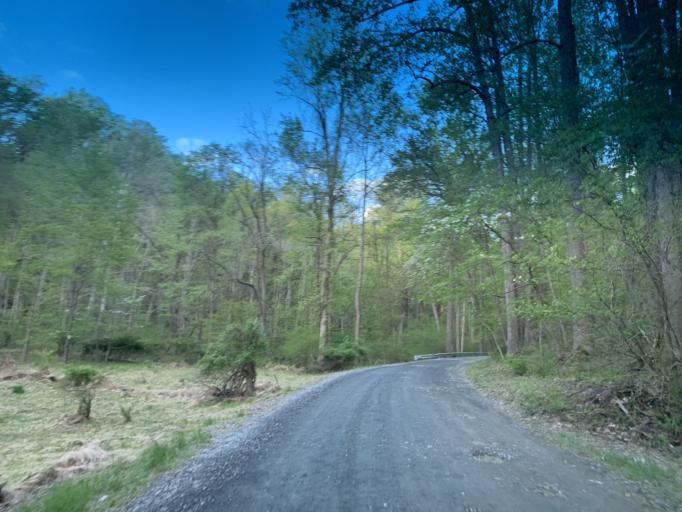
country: US
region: Maryland
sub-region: Harford County
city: Jarrettsville
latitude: 39.6295
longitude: -76.4243
